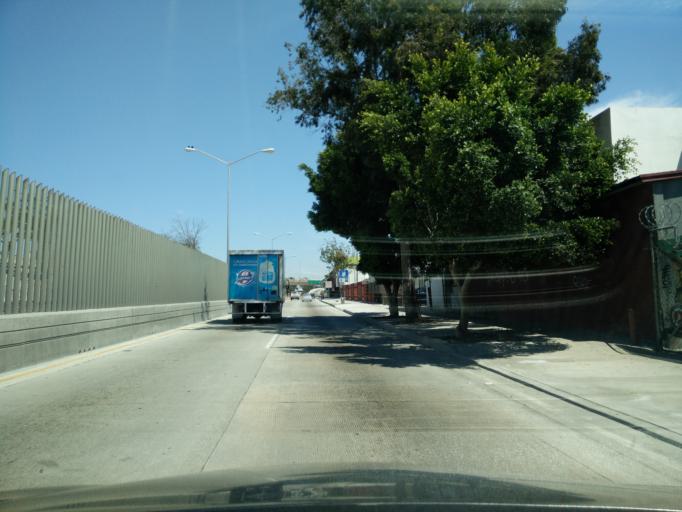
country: MX
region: Baja California
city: Tijuana
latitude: 32.5396
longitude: -117.0355
